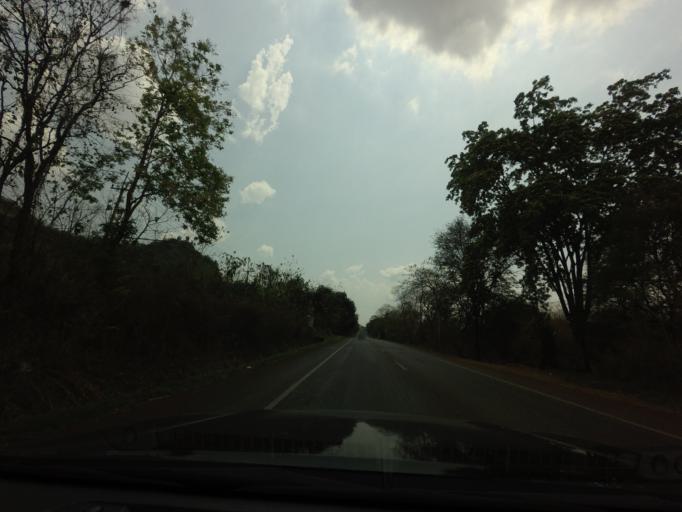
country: TH
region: Kanchanaburi
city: Sai Yok
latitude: 14.1468
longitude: 99.1450
